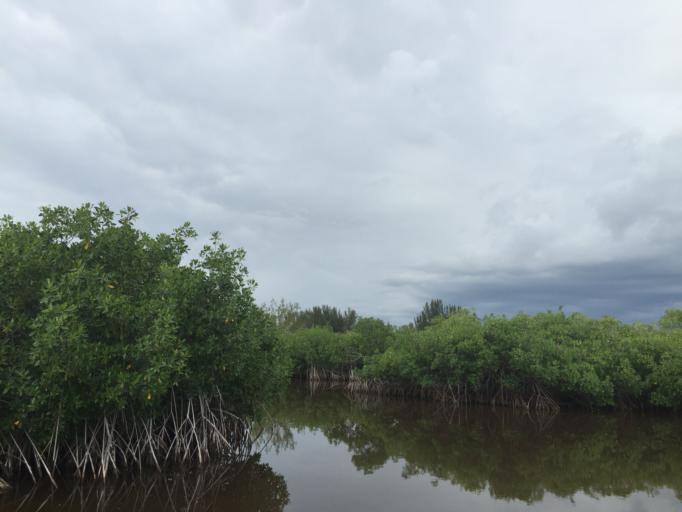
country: US
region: Florida
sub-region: Collier County
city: Marco
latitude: 25.9121
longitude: -81.3708
